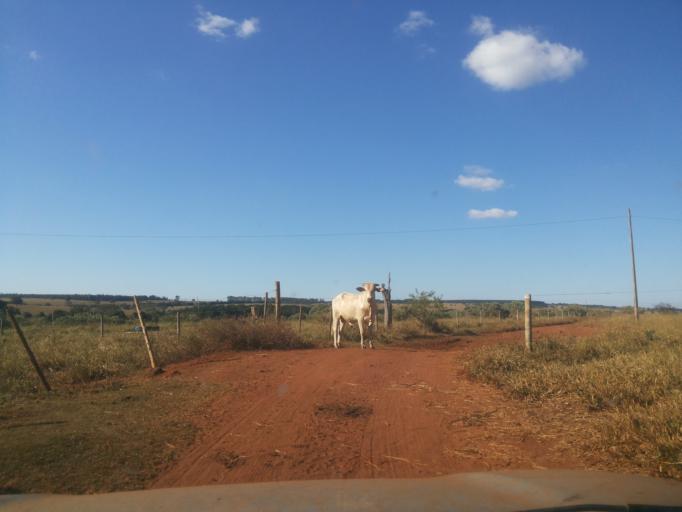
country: BR
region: Minas Gerais
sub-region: Centralina
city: Centralina
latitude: -18.7366
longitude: -49.1803
